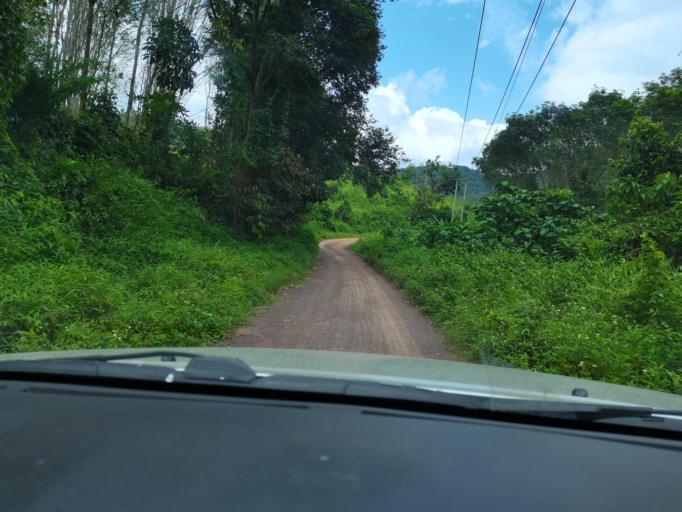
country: LA
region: Loungnamtha
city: Muang Long
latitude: 20.7007
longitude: 101.0310
